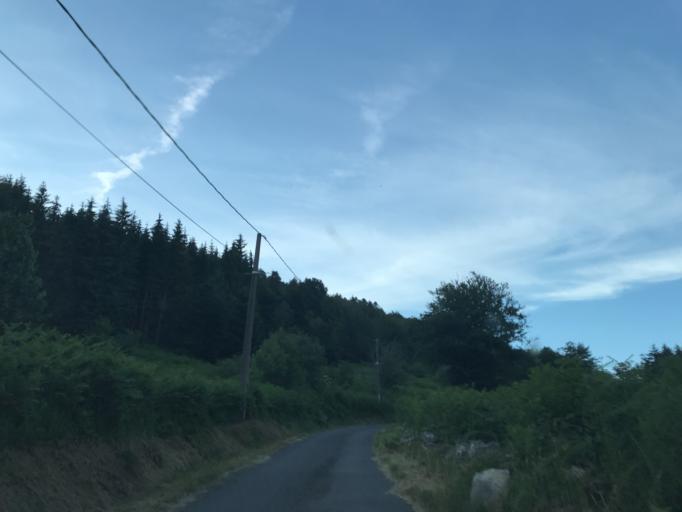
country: FR
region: Rhone-Alpes
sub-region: Departement de la Loire
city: Noiretable
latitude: 45.7991
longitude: 3.7029
